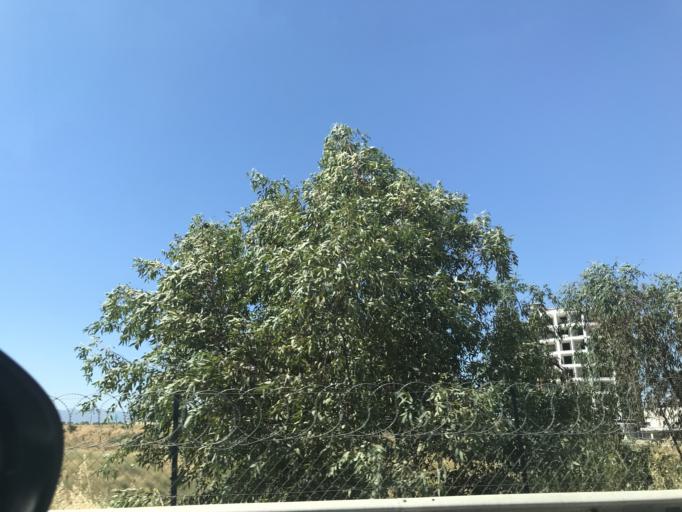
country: TR
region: Aydin
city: Aydin
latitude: 37.8231
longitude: 27.8397
